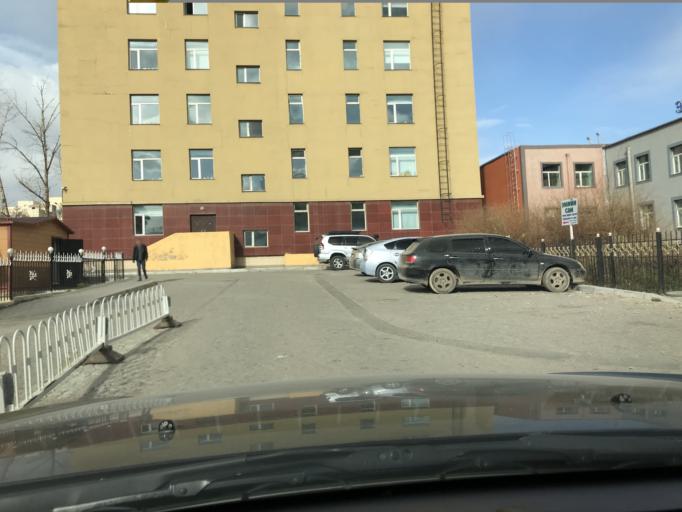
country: MN
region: Ulaanbaatar
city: Ulaanbaatar
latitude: 47.9152
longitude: 106.9676
